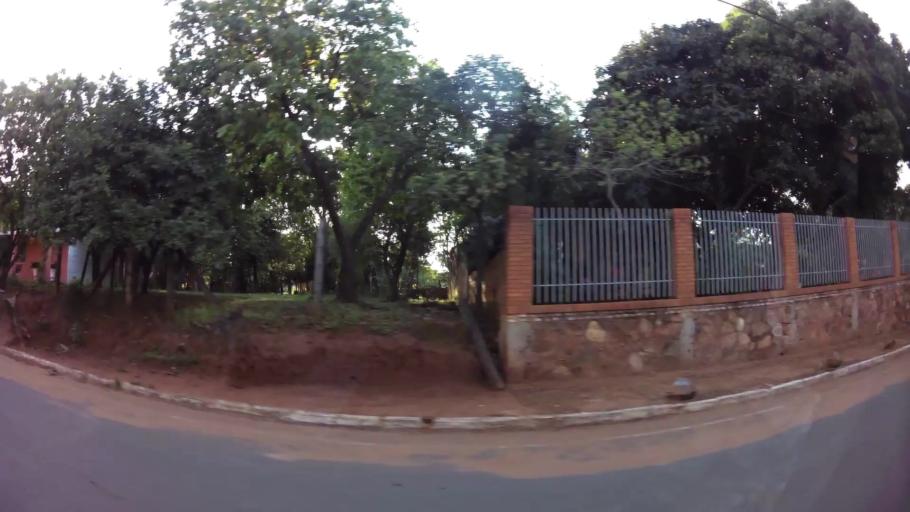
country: PY
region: Central
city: Fernando de la Mora
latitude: -25.3575
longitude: -57.5288
